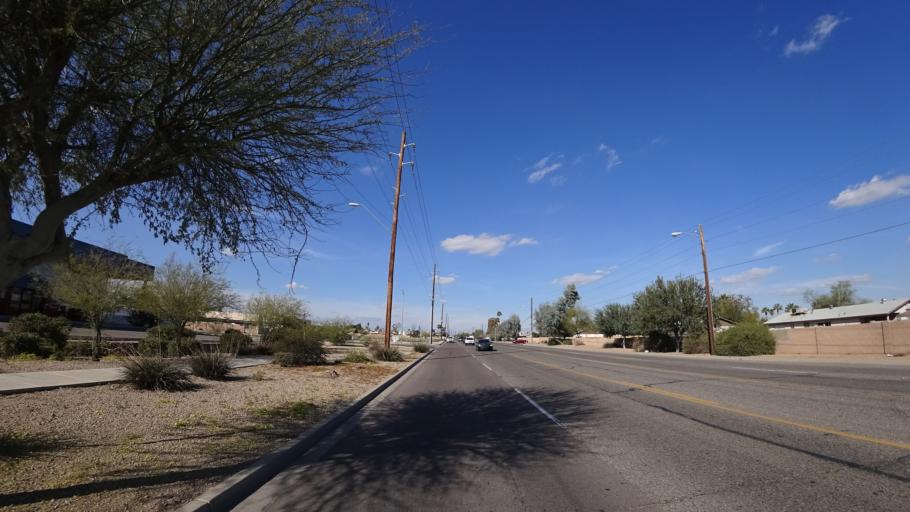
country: US
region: Arizona
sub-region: Maricopa County
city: Peoria
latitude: 33.5710
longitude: -112.2204
